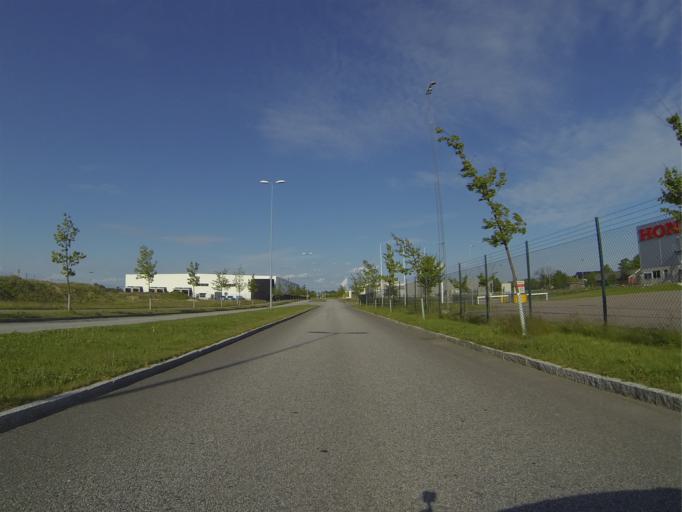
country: SE
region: Skane
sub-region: Burlovs Kommun
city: Arloev
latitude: 55.6163
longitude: 13.1046
